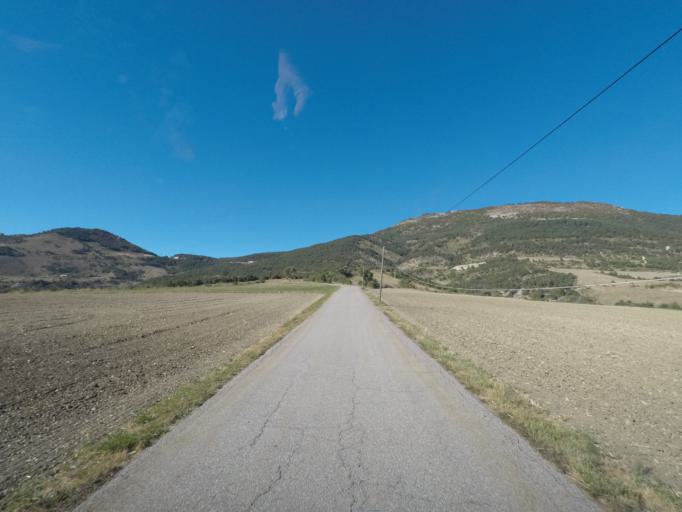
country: FR
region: Provence-Alpes-Cote d'Azur
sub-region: Departement des Hautes-Alpes
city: Serres
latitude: 44.4218
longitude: 5.5827
